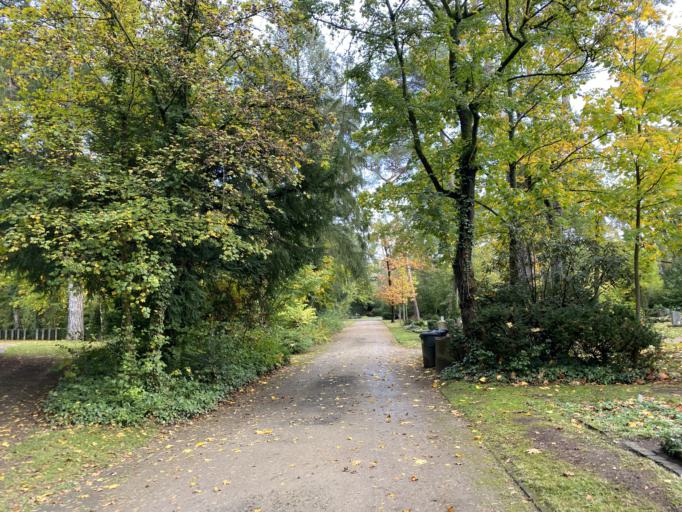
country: DE
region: Hesse
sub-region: Regierungsbezirk Darmstadt
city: Darmstadt
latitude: 49.8719
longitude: 8.6136
